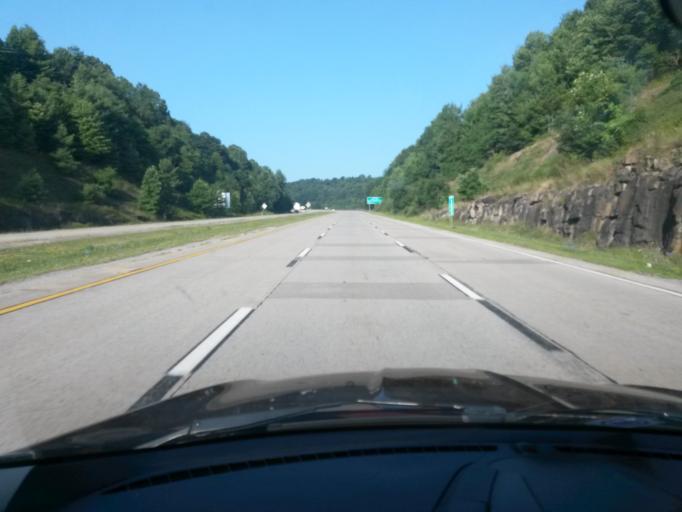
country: US
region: West Virginia
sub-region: Raleigh County
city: Beaver
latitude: 37.7496
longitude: -81.1575
